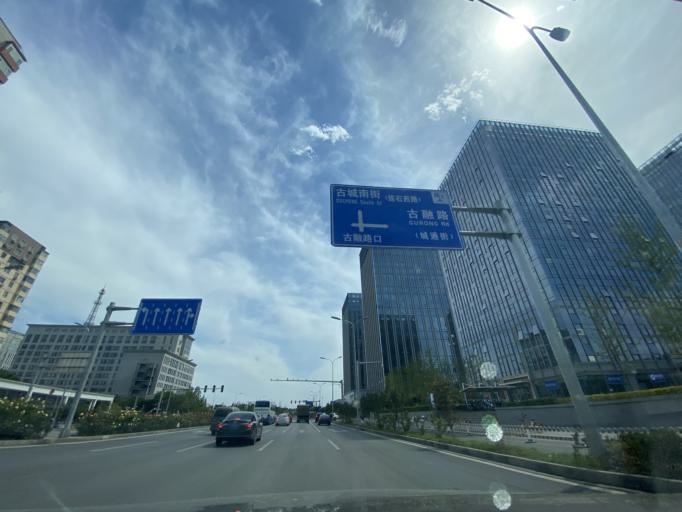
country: CN
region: Beijing
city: Lugu
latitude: 39.9055
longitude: 116.1803
